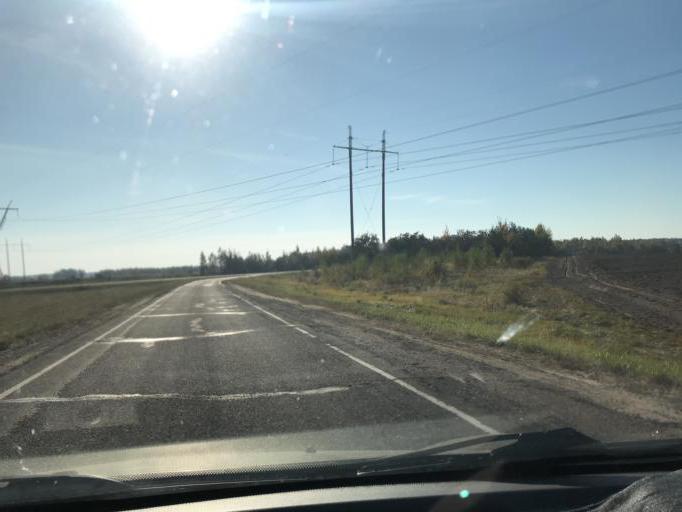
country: BY
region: Mogilev
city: Babruysk
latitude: 53.1067
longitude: 29.0544
